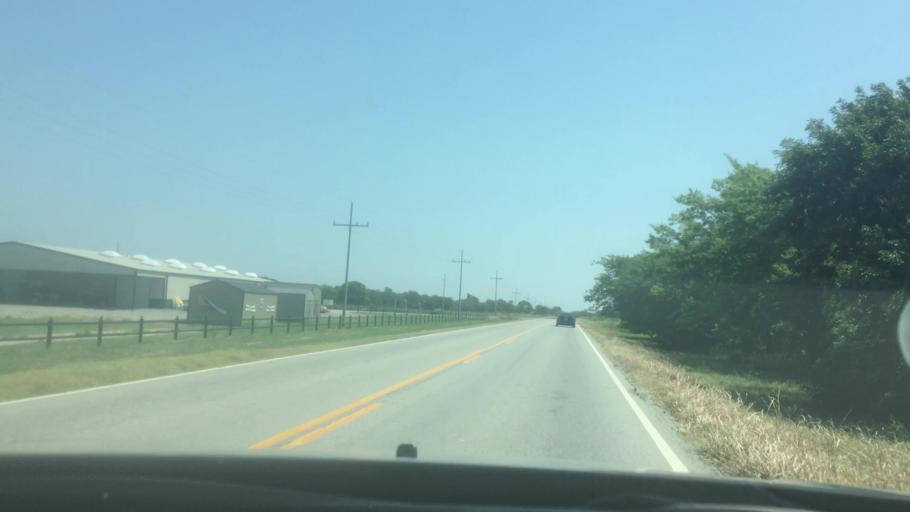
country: US
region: Oklahoma
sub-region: Coal County
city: Coalgate
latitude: 34.4896
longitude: -96.4215
